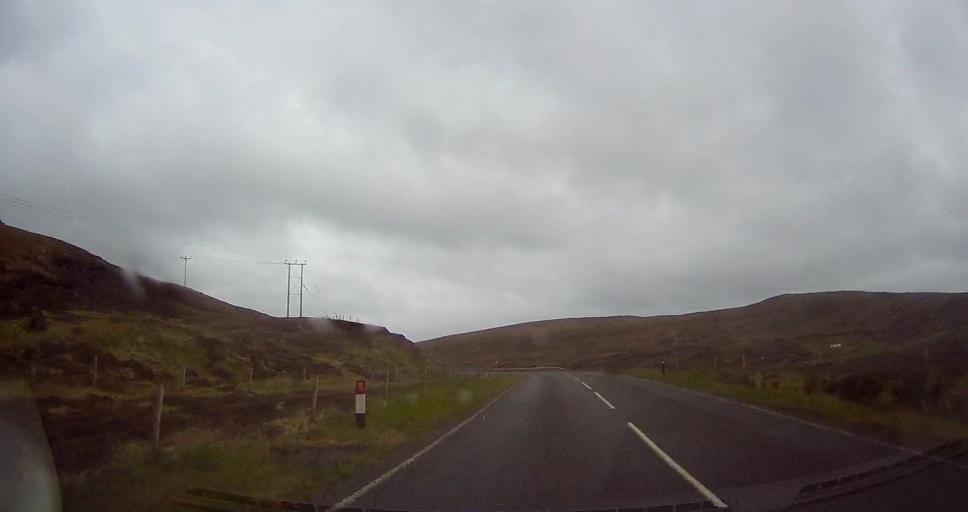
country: GB
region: Scotland
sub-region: Shetland Islands
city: Lerwick
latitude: 60.4415
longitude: -1.3962
